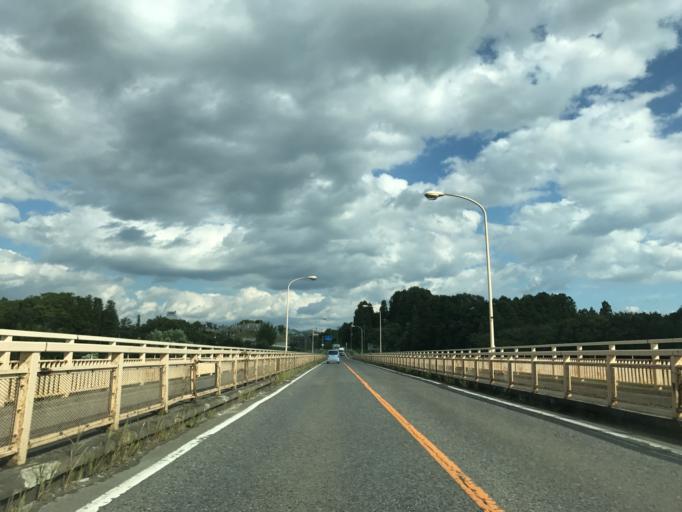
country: JP
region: Fukushima
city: Koriyama
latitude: 37.4071
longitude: 140.4084
